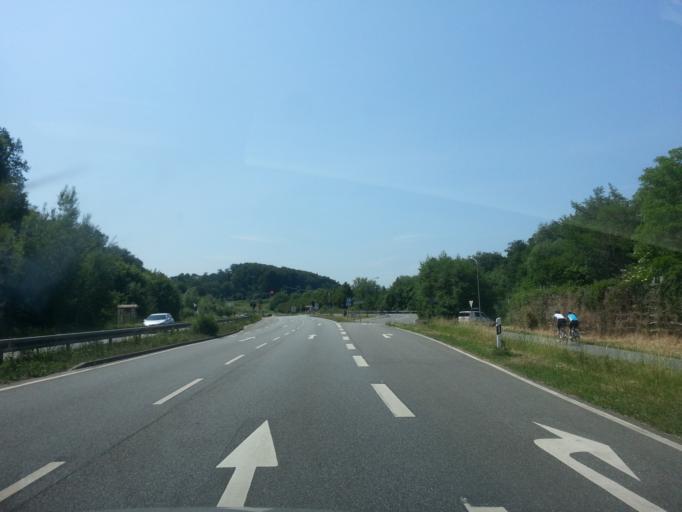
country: DE
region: Hesse
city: Ober-Ramstadt
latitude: 49.8279
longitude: 8.7230
